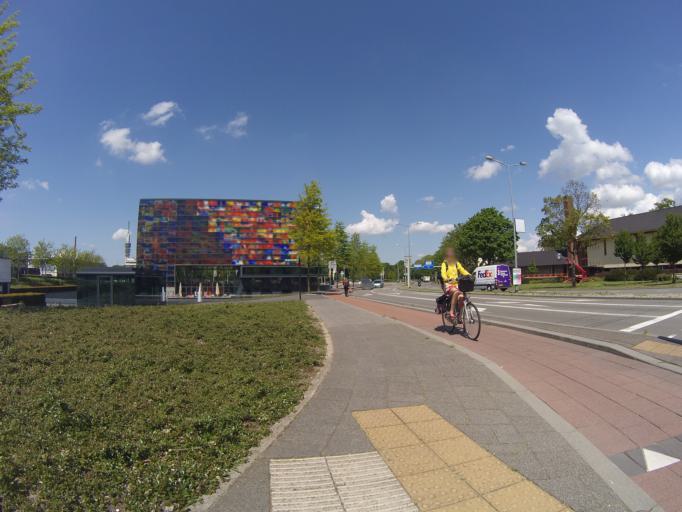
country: NL
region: North Holland
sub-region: Gemeente Hilversum
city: Hilversum
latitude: 52.2344
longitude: 5.1736
